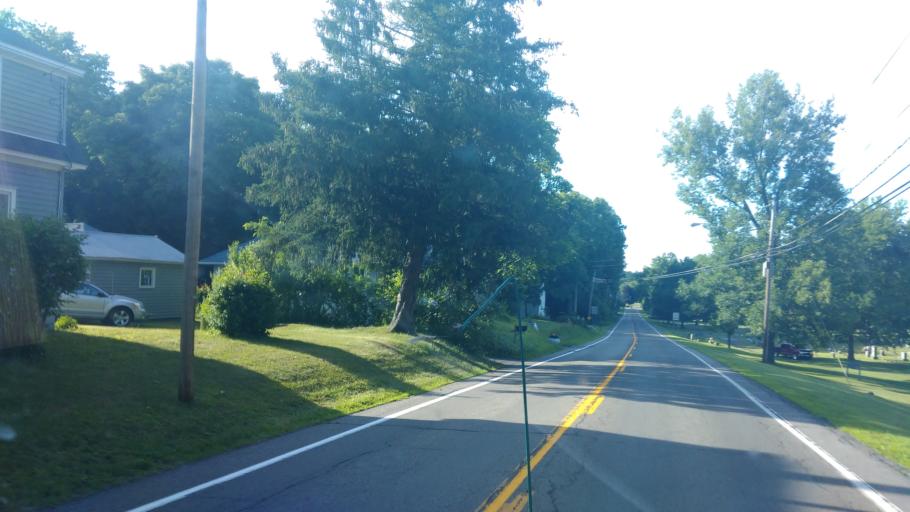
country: US
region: New York
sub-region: Wayne County
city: Lyons
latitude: 43.0733
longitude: -76.9895
